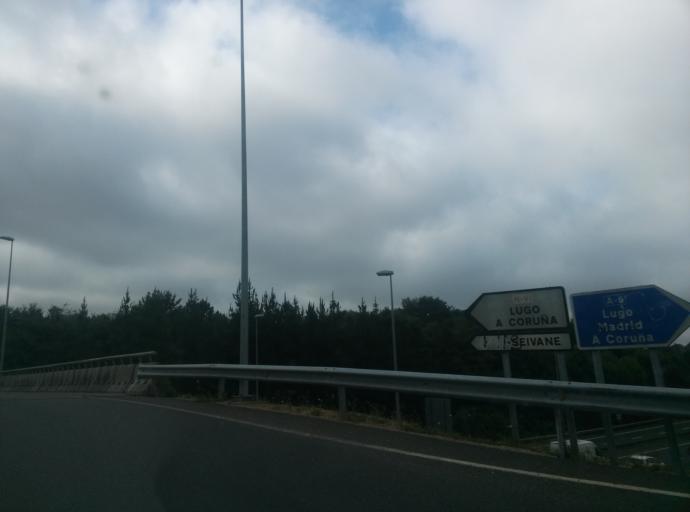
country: ES
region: Galicia
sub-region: Provincia de Lugo
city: Lugo
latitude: 43.0533
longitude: -7.5636
